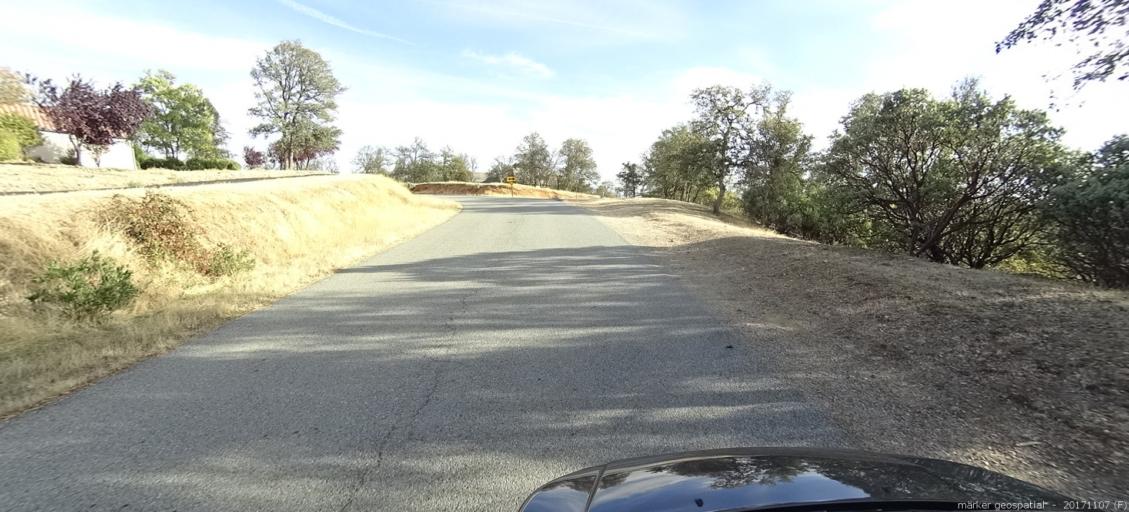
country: US
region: California
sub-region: Shasta County
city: Shasta
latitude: 40.5077
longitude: -122.4728
